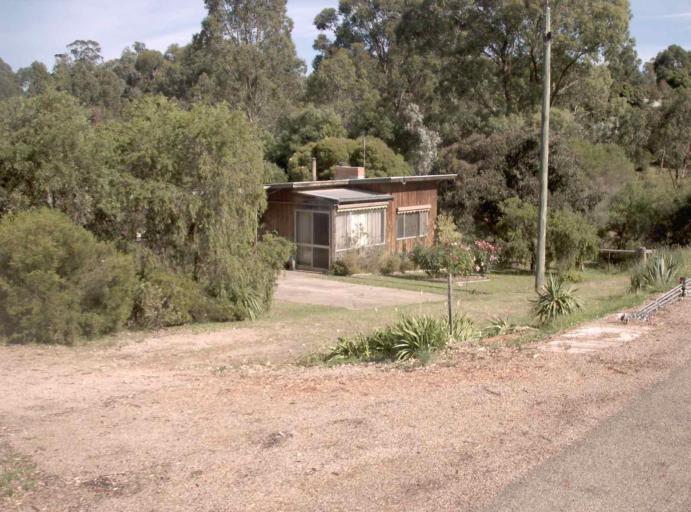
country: AU
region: Victoria
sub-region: East Gippsland
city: Bairnsdale
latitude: -37.7159
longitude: 147.8055
